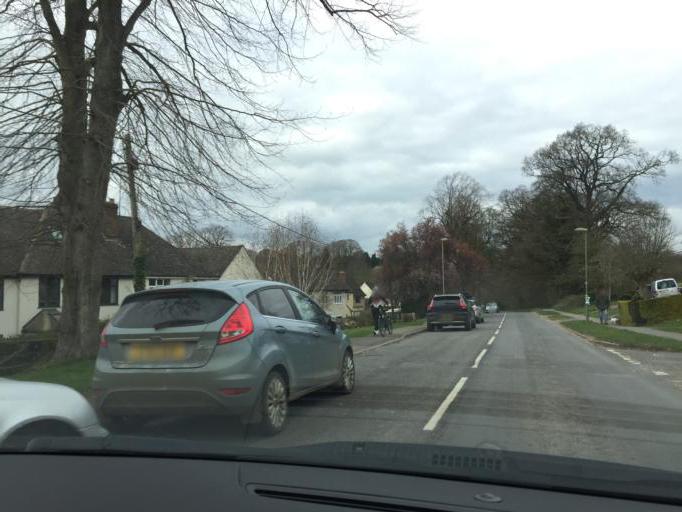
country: GB
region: England
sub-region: Oxfordshire
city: Chipping Norton
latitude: 51.9470
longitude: -1.5431
